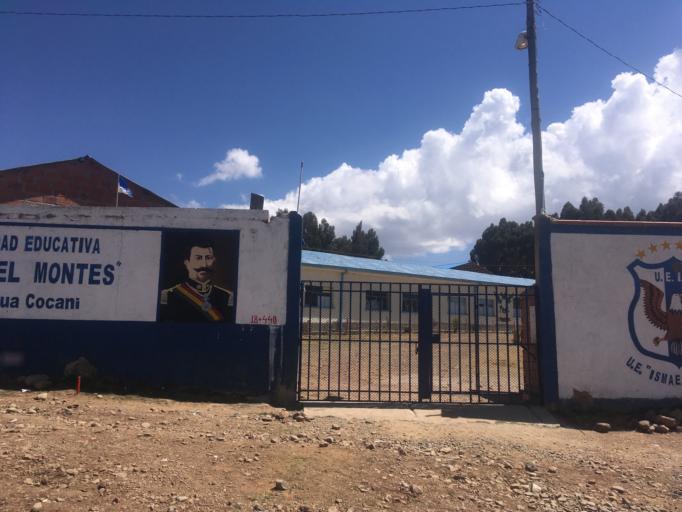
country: BO
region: La Paz
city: Huatajata
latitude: -16.1898
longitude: -68.7492
